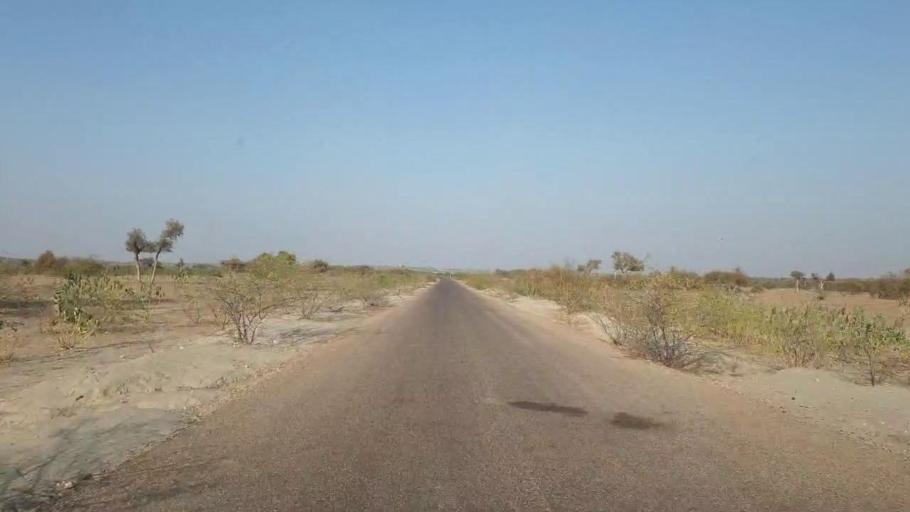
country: PK
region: Sindh
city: Chor
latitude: 25.5842
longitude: 69.8252
